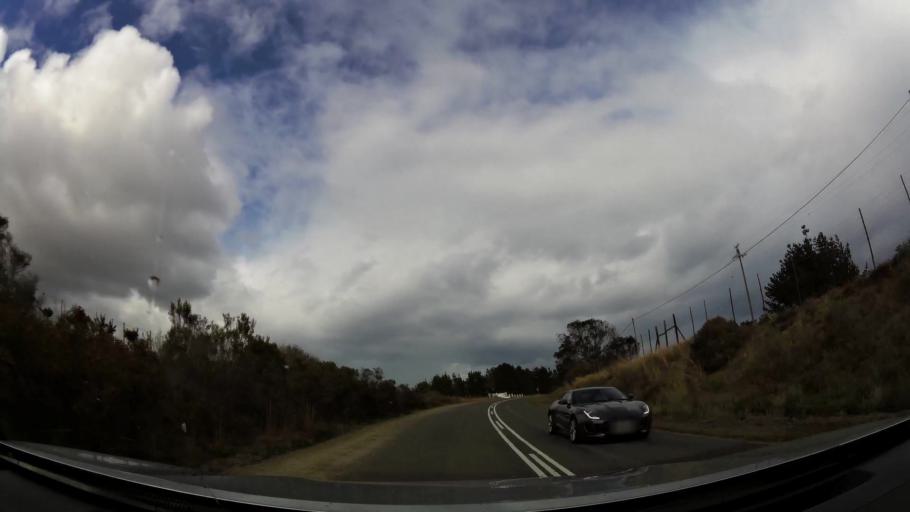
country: ZA
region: Western Cape
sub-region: Eden District Municipality
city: George
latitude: -34.0380
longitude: 22.3244
